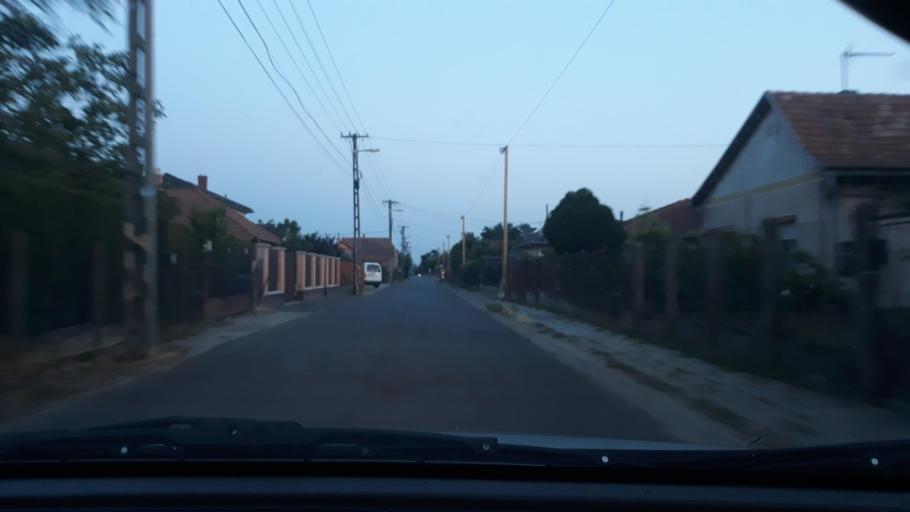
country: HU
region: Hajdu-Bihar
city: Debrecen
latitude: 47.5364
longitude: 21.6660
